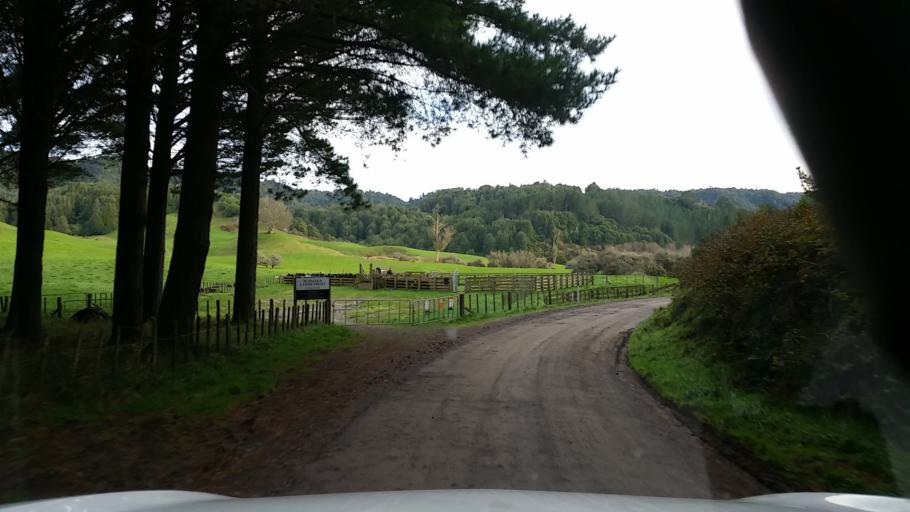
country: NZ
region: Bay of Plenty
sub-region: Rotorua District
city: Rotorua
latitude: -38.2203
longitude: 176.1597
